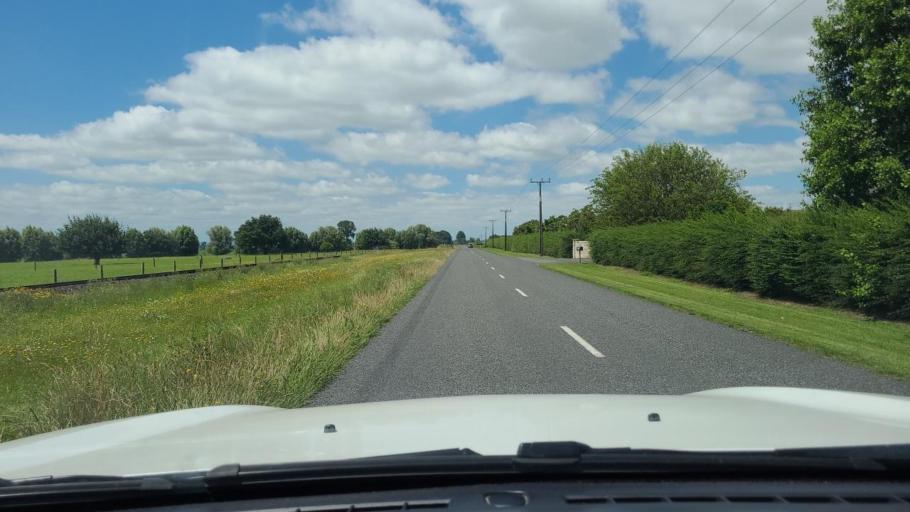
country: NZ
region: Waikato
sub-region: Matamata-Piako District
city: Matamata
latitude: -37.8674
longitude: 175.7554
